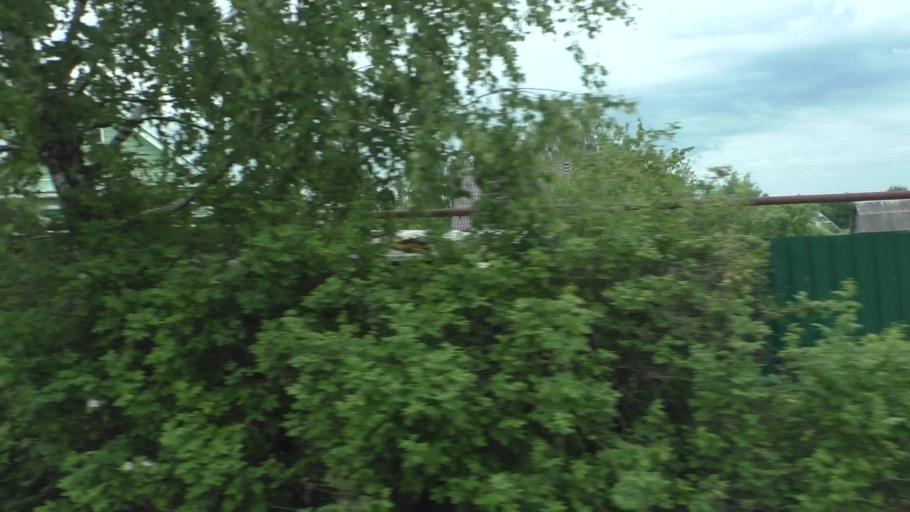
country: RU
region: Moskovskaya
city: Il'inskiy Pogost
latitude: 55.4697
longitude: 38.8967
